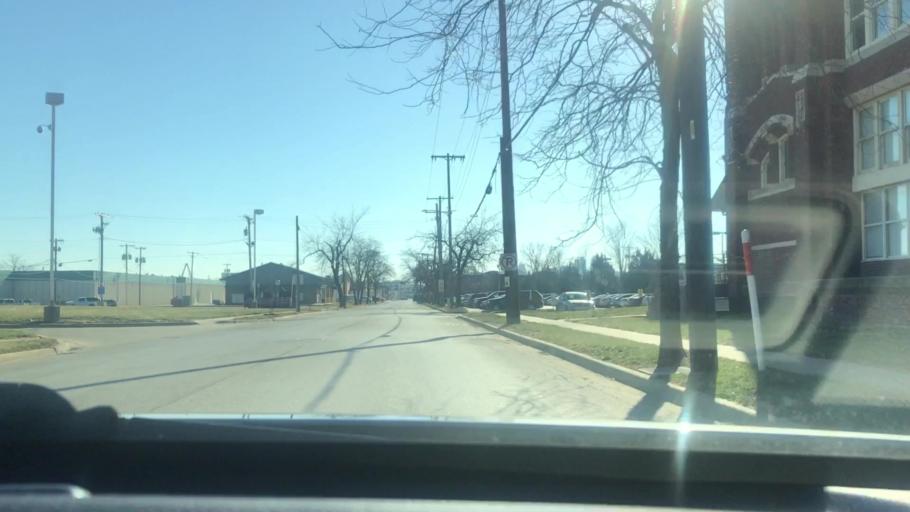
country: US
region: Missouri
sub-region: Clay County
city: North Kansas City
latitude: 39.1423
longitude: -94.5715
